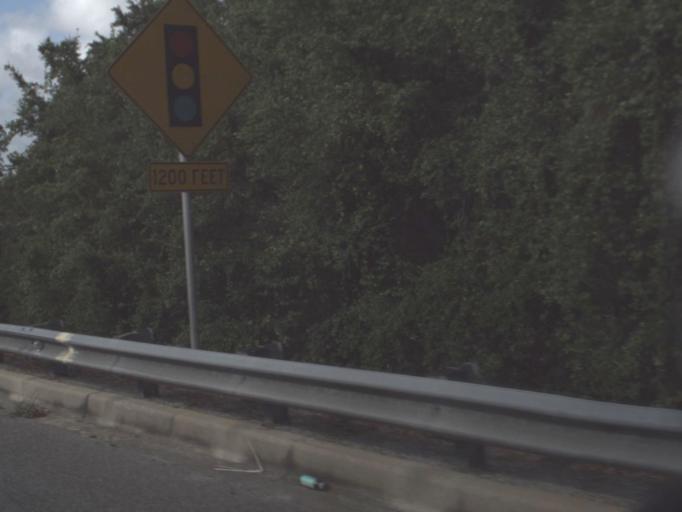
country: US
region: Florida
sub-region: Lake County
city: Lady Lake
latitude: 28.9272
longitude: -81.9252
